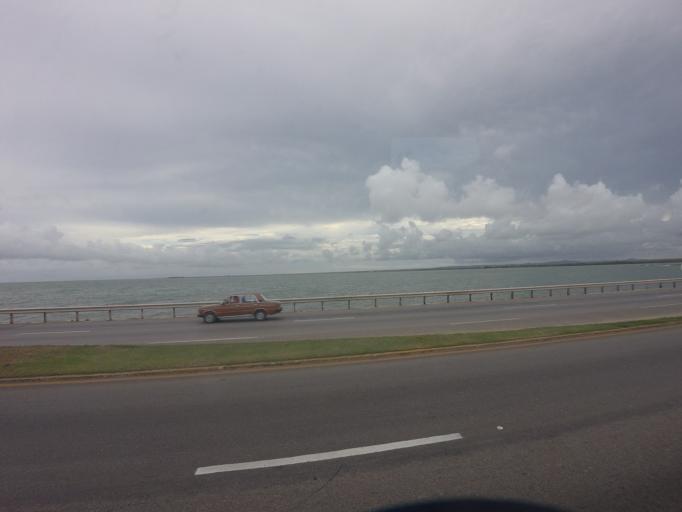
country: CU
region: Matanzas
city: Varadero
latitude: 23.1442
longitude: -81.2647
